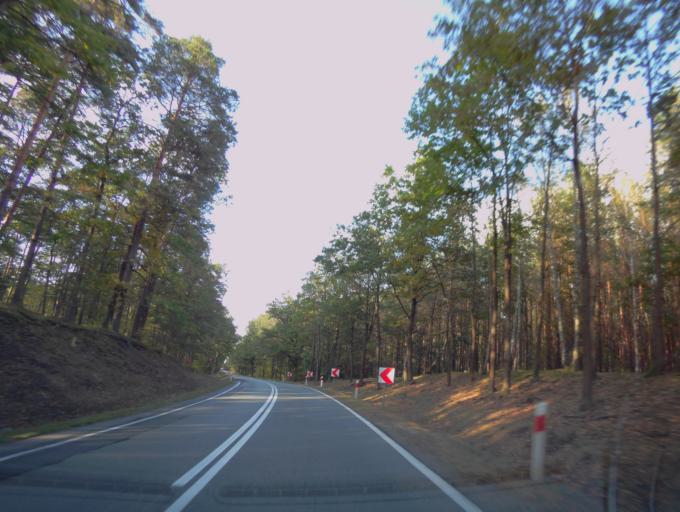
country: PL
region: Subcarpathian Voivodeship
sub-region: Powiat nizanski
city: Krzeszow
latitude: 50.3850
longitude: 22.3081
